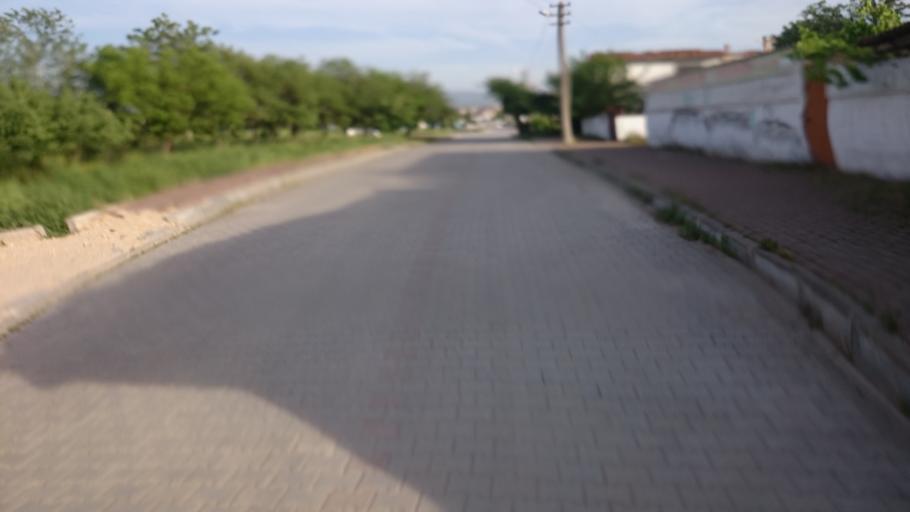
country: TR
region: Bursa
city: Niluefer
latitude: 40.2357
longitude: 28.9100
